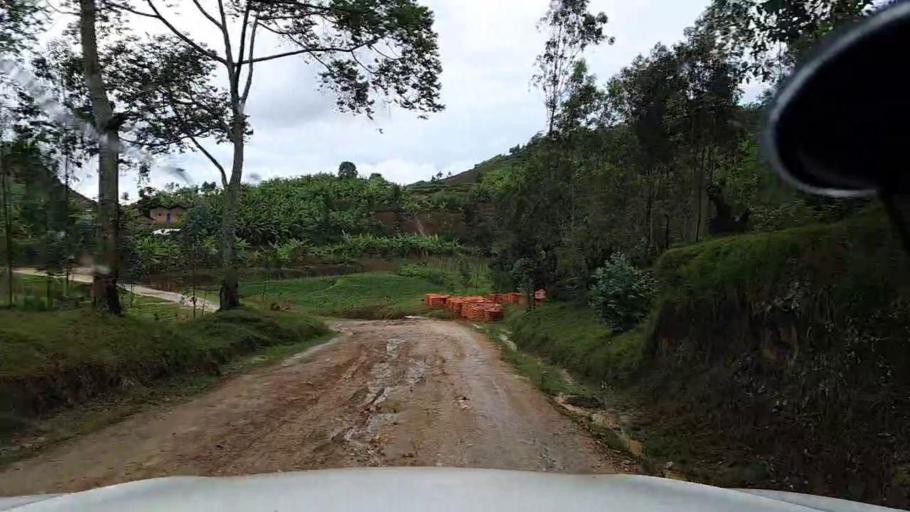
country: RW
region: Western Province
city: Kibuye
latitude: -2.1200
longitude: 29.4934
